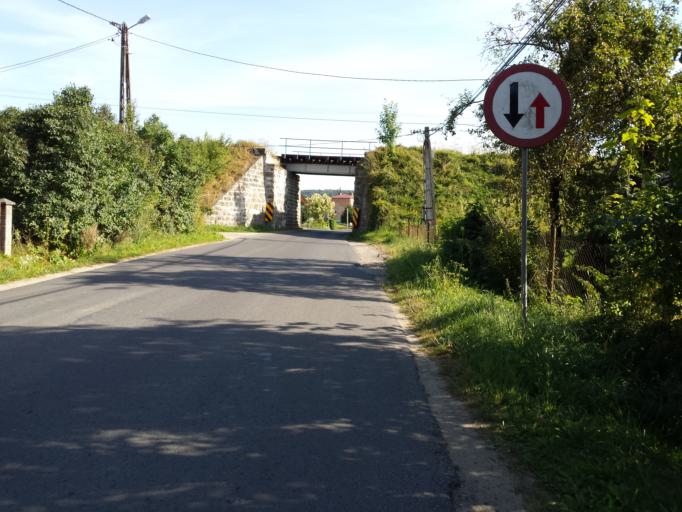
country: PL
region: Subcarpathian Voivodeship
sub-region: Powiat leski
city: Olszanica
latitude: 49.4799
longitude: 22.4432
